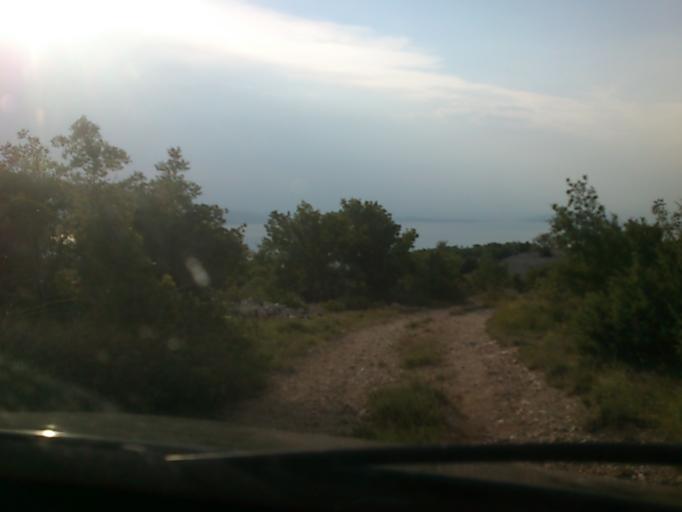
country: HR
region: Primorsko-Goranska
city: Banjol
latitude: 44.7629
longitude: 14.8964
